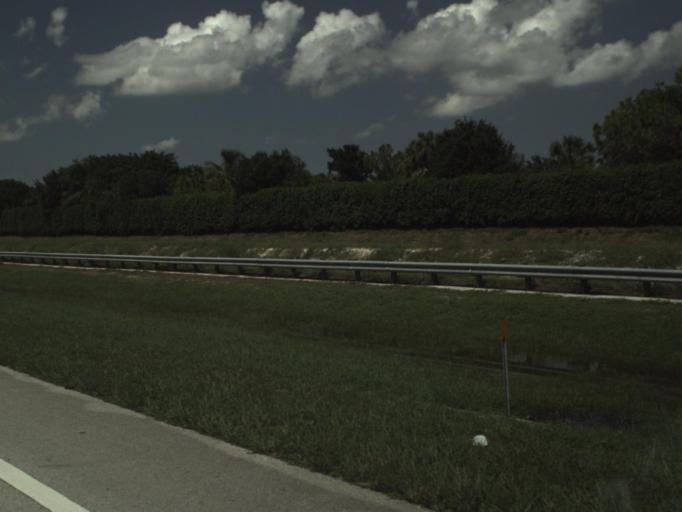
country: US
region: Florida
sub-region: Palm Beach County
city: Wellington
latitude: 26.6041
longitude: -80.2053
